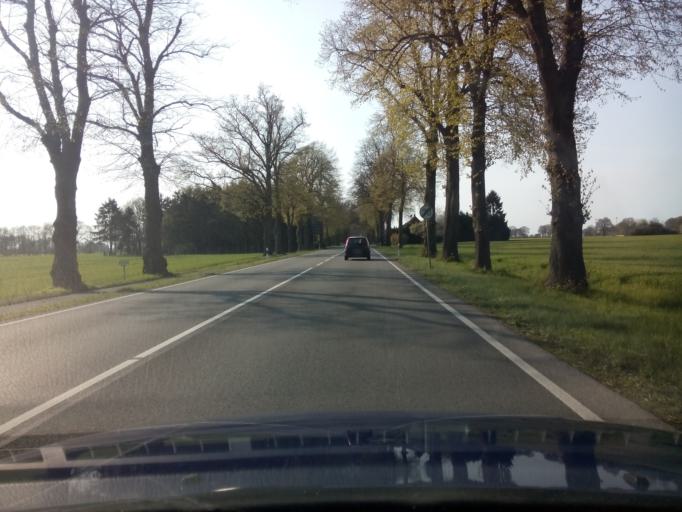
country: DE
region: Lower Saxony
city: Bruchhausen-Vilsen
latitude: 52.8137
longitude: 8.9577
